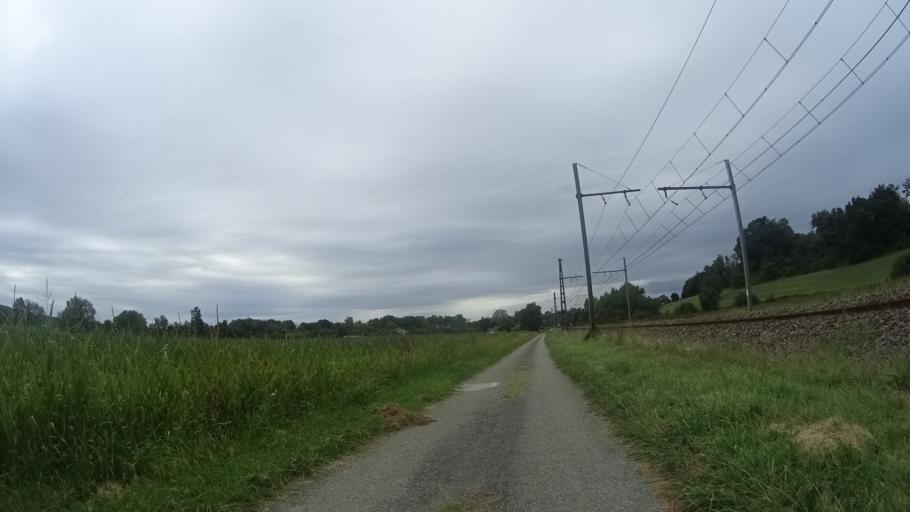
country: FR
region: Aquitaine
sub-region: Departement des Pyrenees-Atlantiques
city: Orthez
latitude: 43.4682
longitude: -0.7223
